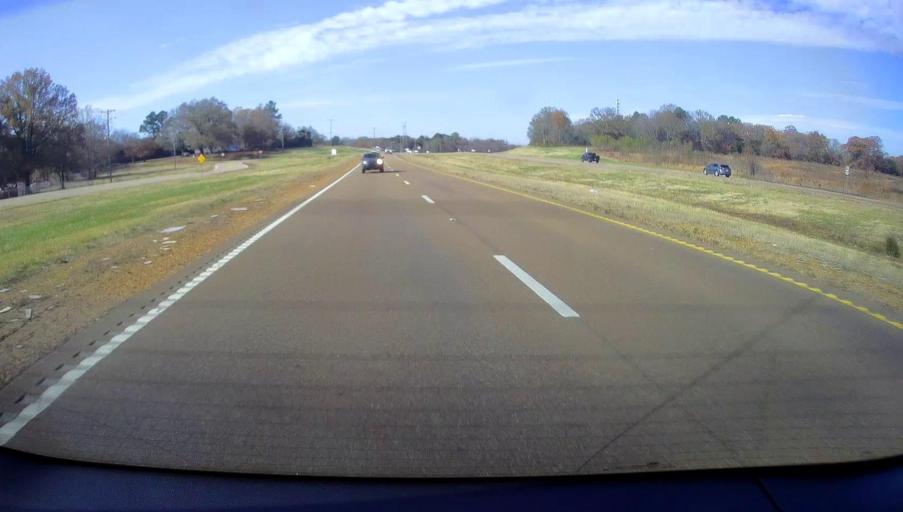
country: US
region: Tennessee
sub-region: Fayette County
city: Piperton
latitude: 34.9881
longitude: -89.6064
